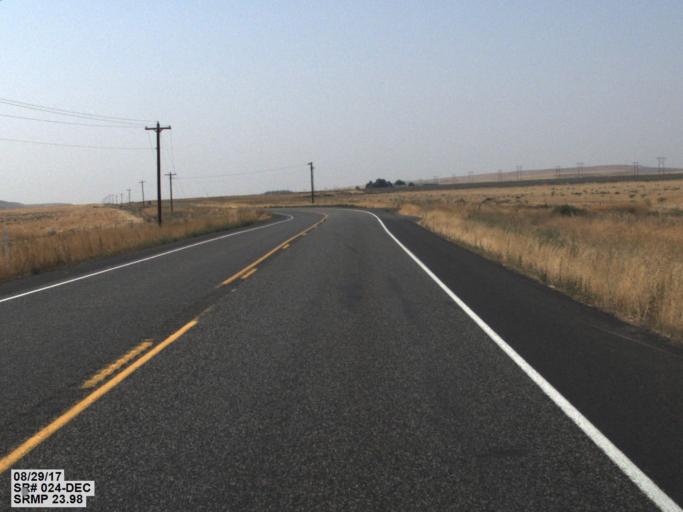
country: US
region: Washington
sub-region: Grant County
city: Desert Aire
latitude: 46.5198
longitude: -120.0109
